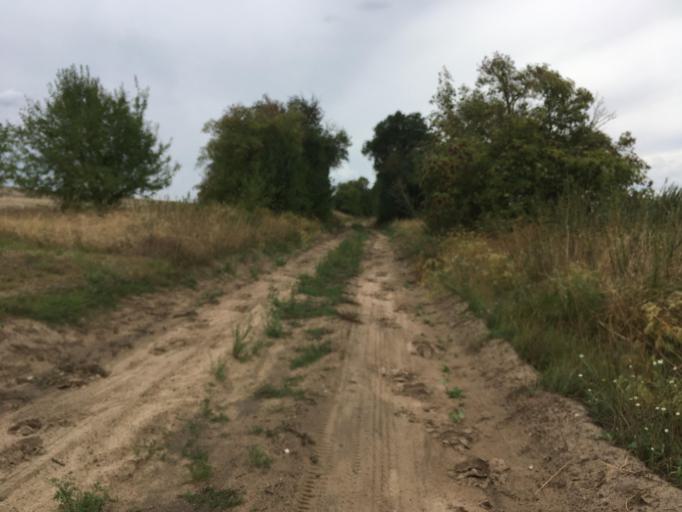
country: DE
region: Brandenburg
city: Passow
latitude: 53.1337
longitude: 14.1109
